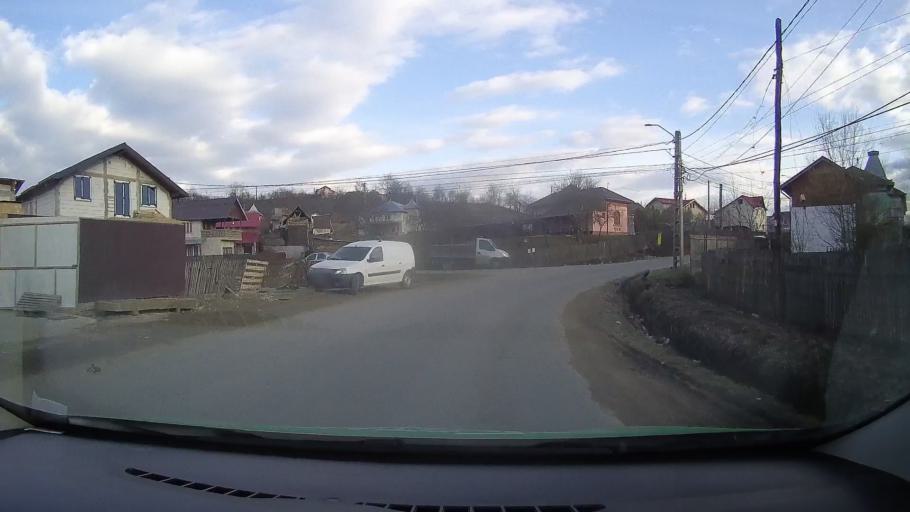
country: RO
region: Dambovita
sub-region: Comuna Ocnita
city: Ocnita
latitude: 44.9835
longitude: 25.5550
